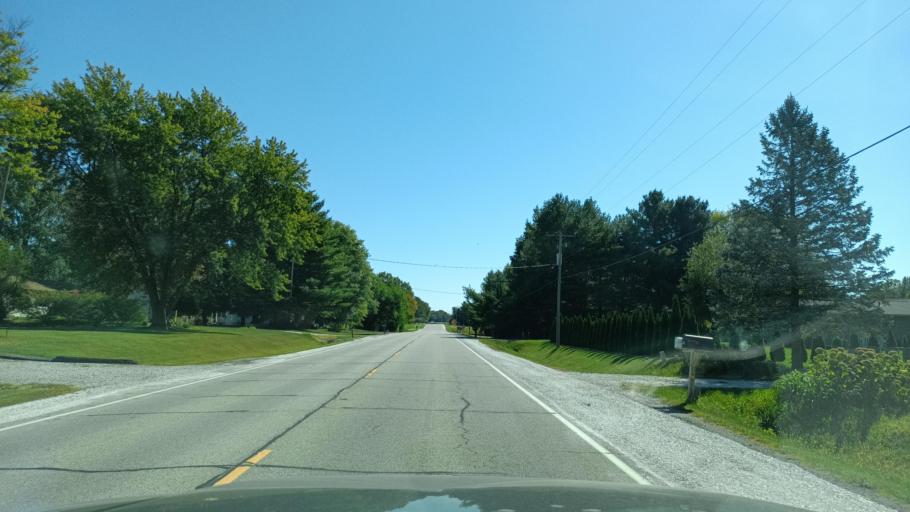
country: US
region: Illinois
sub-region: Peoria County
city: Hanna City
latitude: 40.7930
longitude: -89.7706
